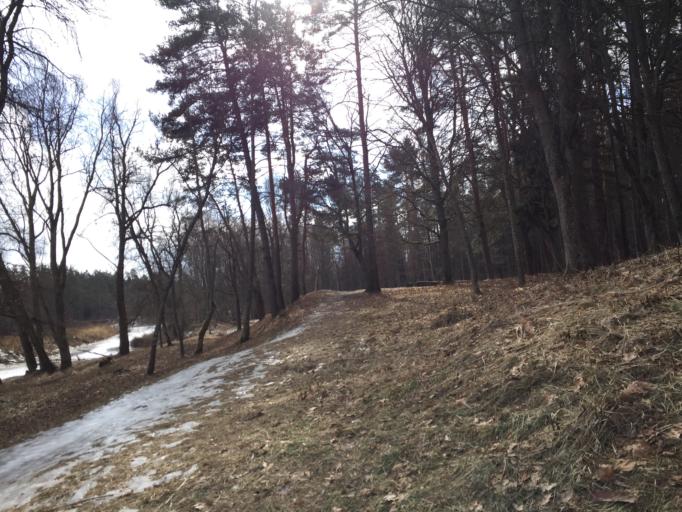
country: LV
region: Valmieras Rajons
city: Valmiera
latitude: 57.5379
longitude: 25.4444
